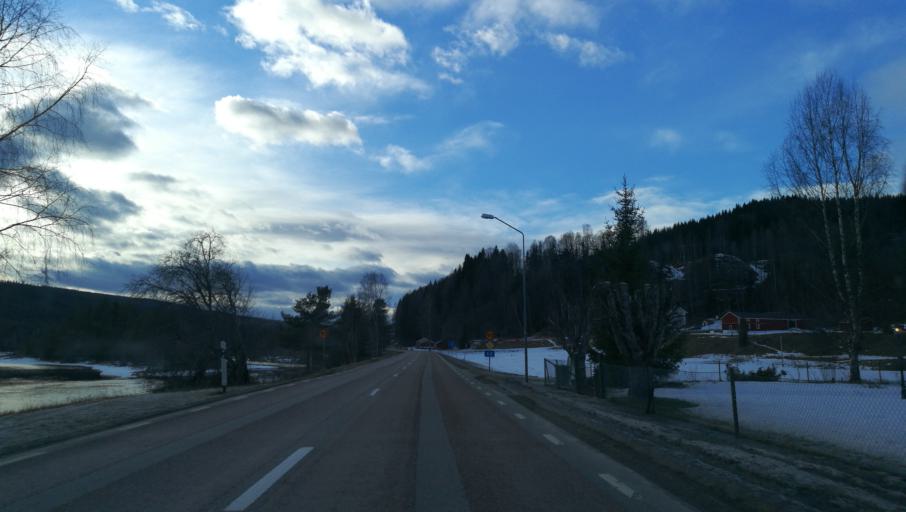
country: SE
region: Vaermland
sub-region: Torsby Kommun
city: Torsby
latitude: 60.7392
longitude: 12.8508
